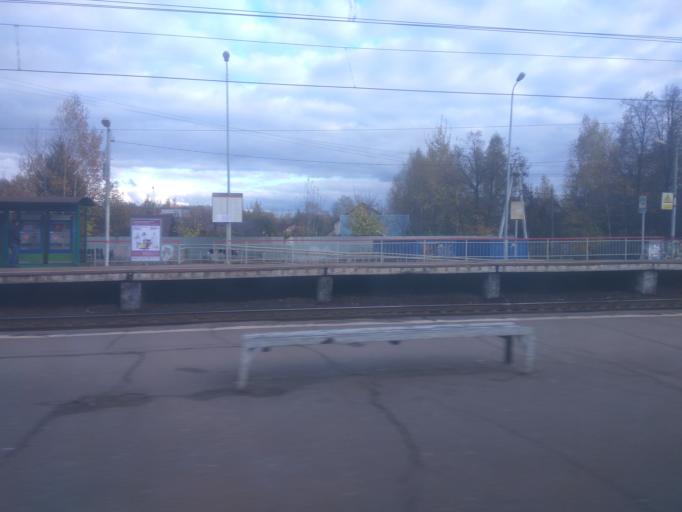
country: RU
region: Moskovskaya
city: Lesnoy Gorodok
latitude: 55.6300
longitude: 37.2177
